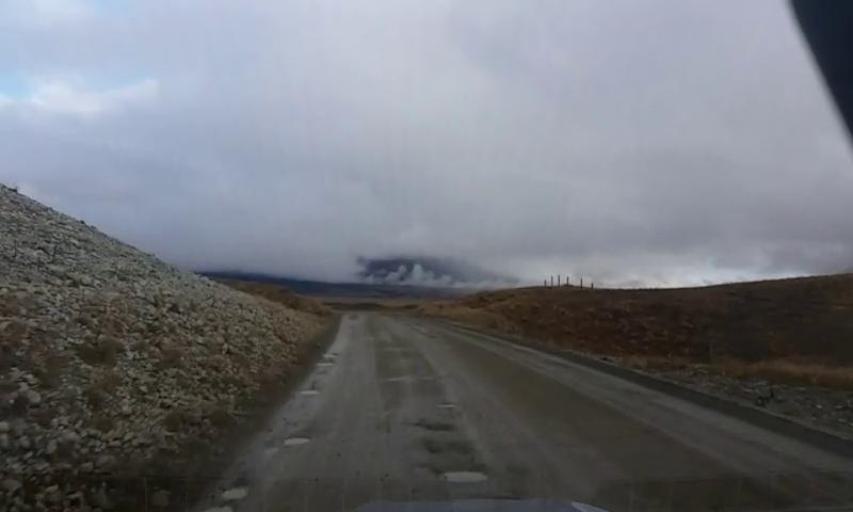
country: NZ
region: Canterbury
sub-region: Ashburton District
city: Methven
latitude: -43.6160
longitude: 171.1341
